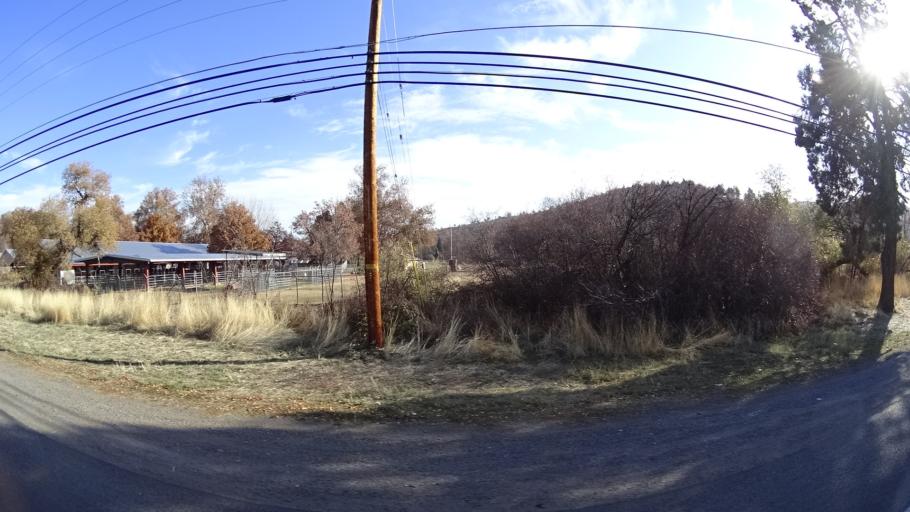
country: US
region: California
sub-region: Siskiyou County
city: Yreka
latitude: 41.7029
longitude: -122.6408
